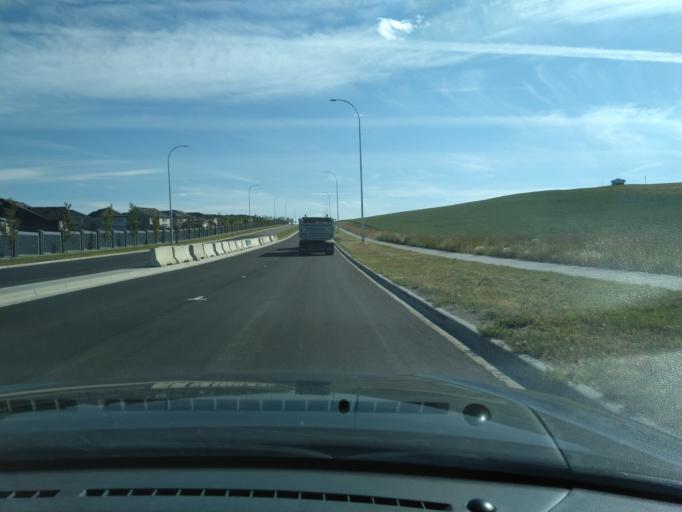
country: CA
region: Alberta
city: Calgary
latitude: 51.1804
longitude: -114.1762
